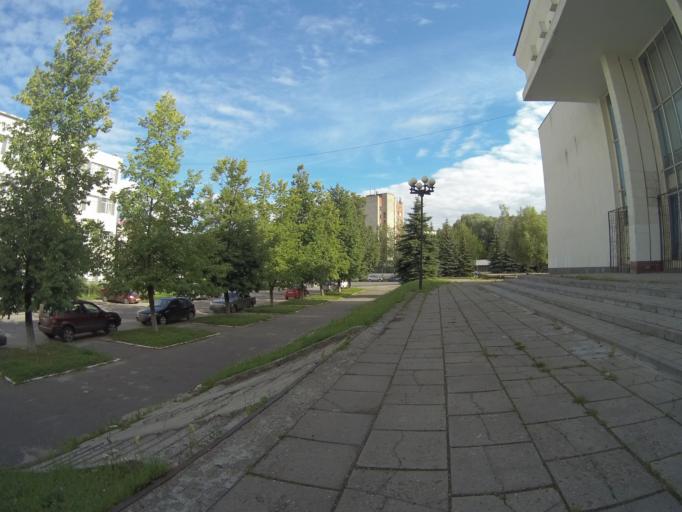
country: RU
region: Vladimir
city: Vladimir
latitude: 56.1515
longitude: 40.4323
